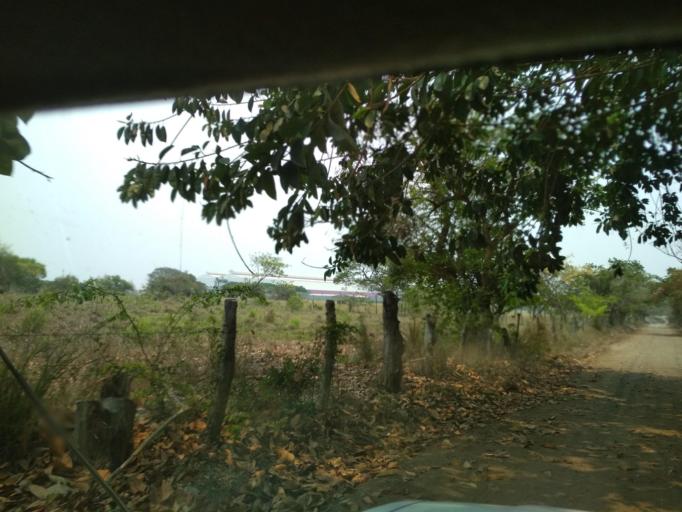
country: MX
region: Veracruz
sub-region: Veracruz
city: Oasis
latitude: 19.1942
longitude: -96.2446
